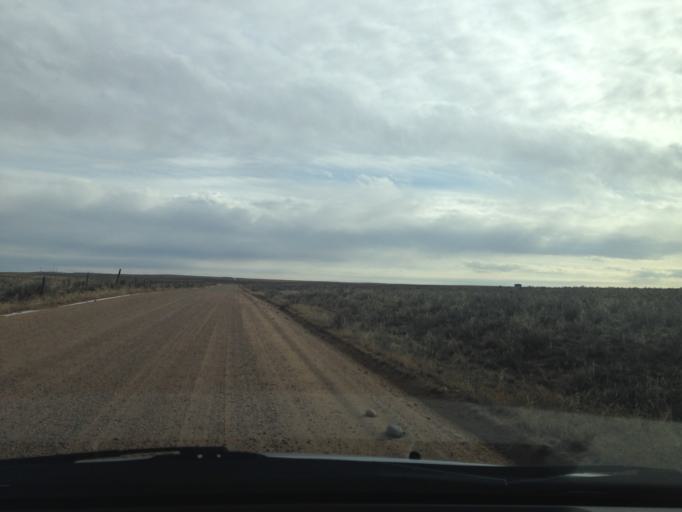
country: US
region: Colorado
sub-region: Weld County
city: Keenesburg
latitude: 40.2815
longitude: -104.2068
